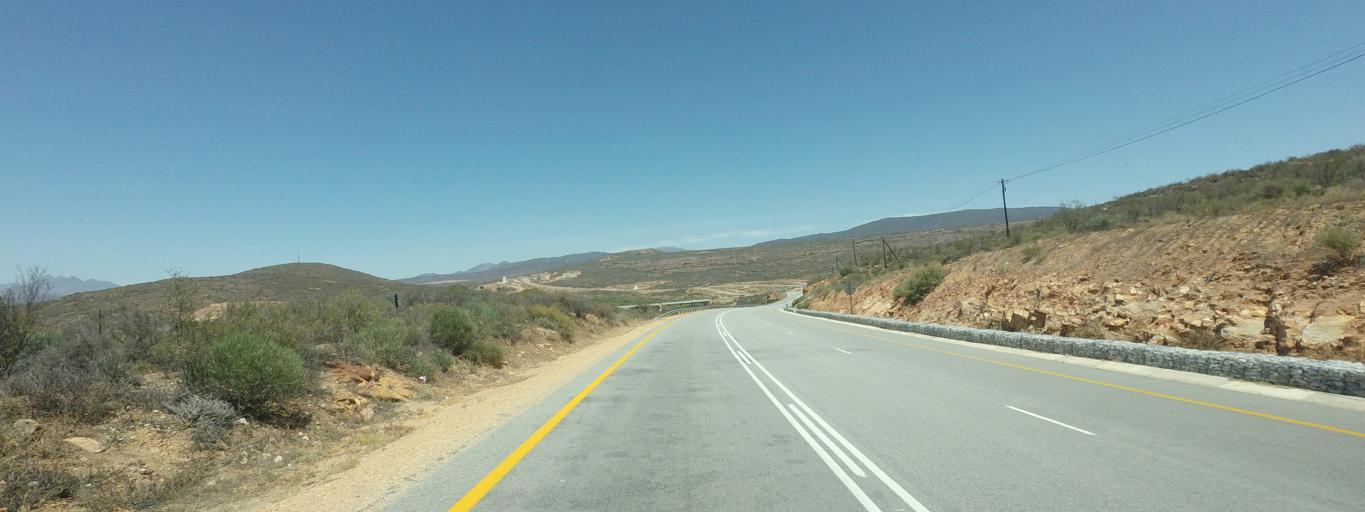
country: ZA
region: Western Cape
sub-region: West Coast District Municipality
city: Clanwilliam
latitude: -32.1659
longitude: 18.8718
